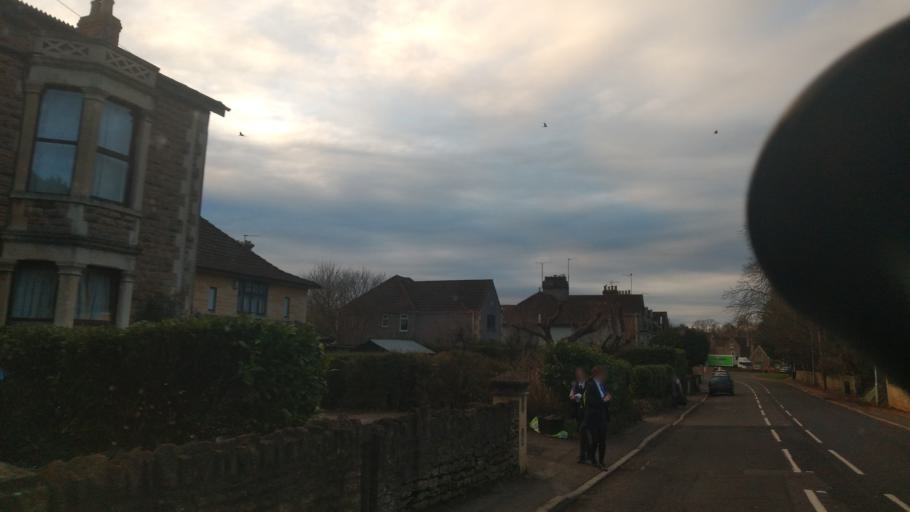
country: GB
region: England
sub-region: Somerset
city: Frome
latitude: 51.2389
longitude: -2.3132
